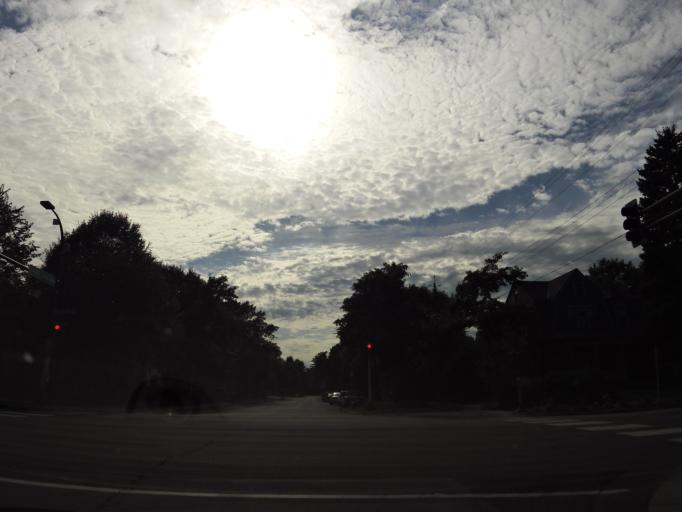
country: US
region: Minnesota
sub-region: Hennepin County
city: Minneapolis
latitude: 44.9910
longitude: -93.2584
